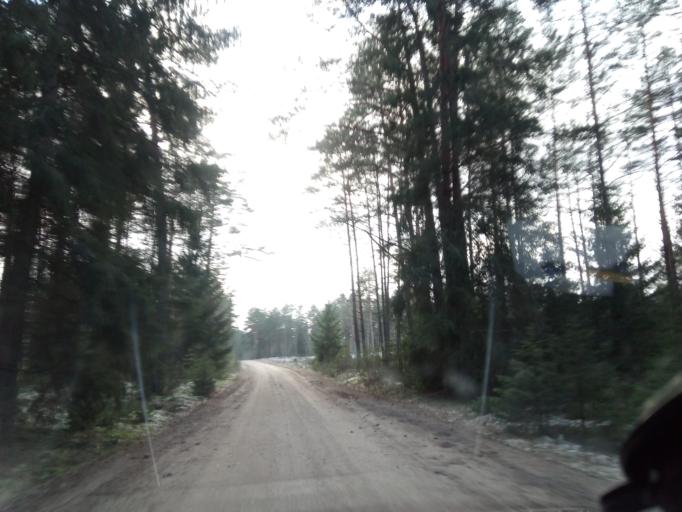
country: LT
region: Alytaus apskritis
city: Varena
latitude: 53.9789
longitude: 24.3316
